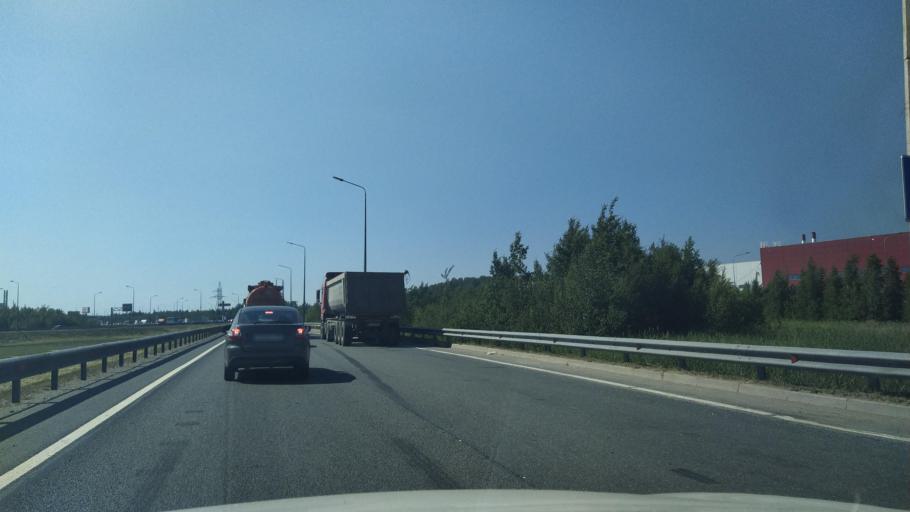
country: RU
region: St.-Petersburg
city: Pargolovo
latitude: 60.1003
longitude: 30.2677
